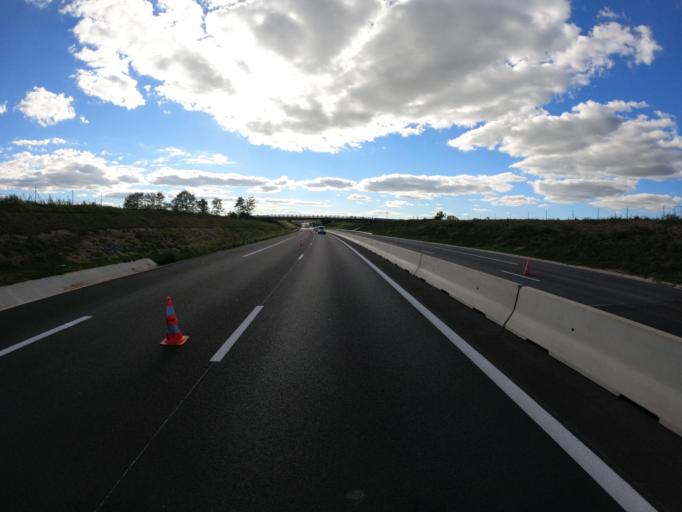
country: FR
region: Auvergne
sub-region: Departement de l'Allier
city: Molinet
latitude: 46.4597
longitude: 3.9433
